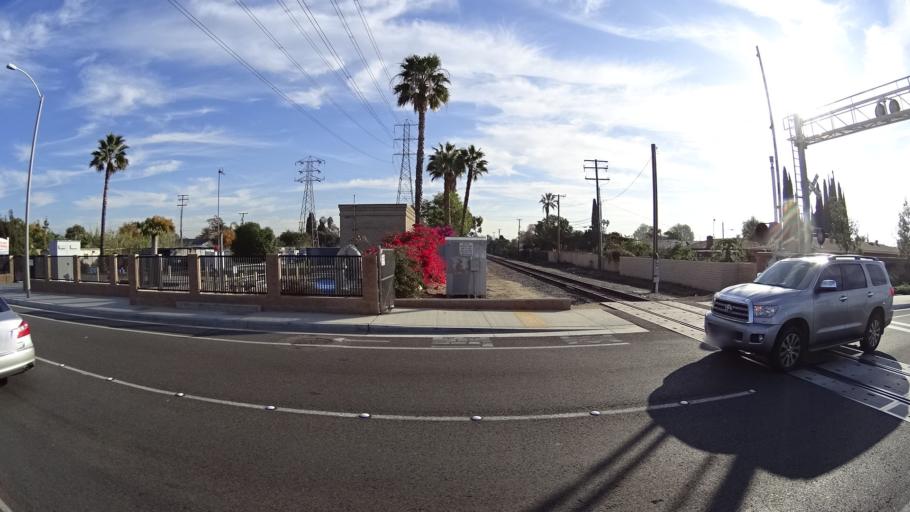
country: US
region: California
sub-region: Orange County
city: Stanton
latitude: 33.8067
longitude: -117.9588
